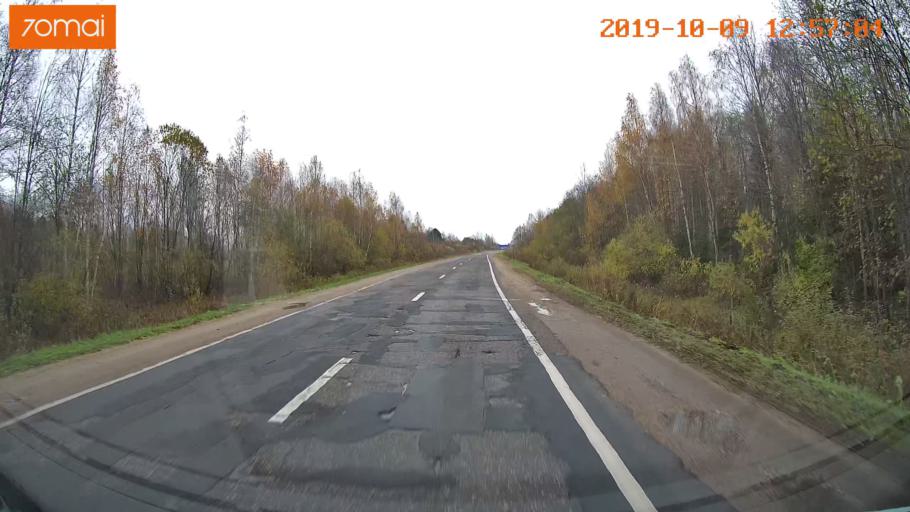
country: RU
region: Jaroslavl
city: Prechistoye
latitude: 58.3935
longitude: 40.4269
